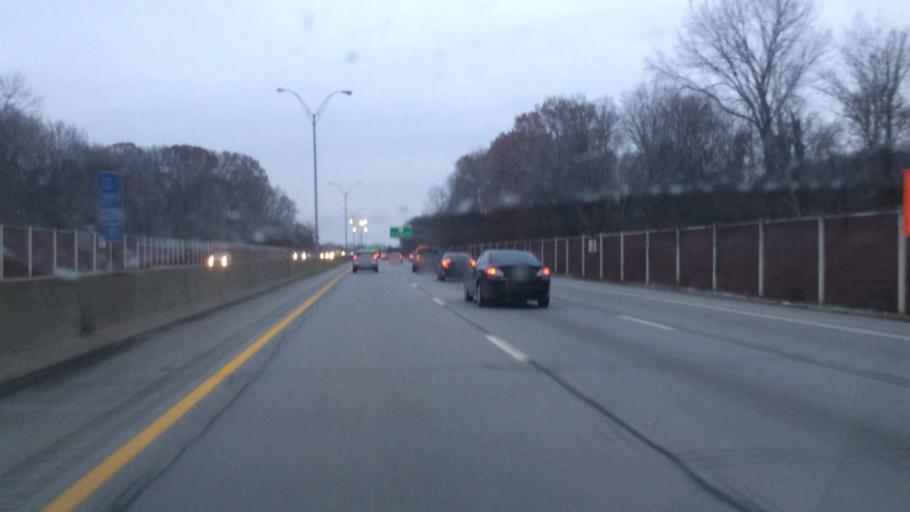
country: US
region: Ohio
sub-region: Summit County
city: Akron
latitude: 41.0731
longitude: -81.5741
